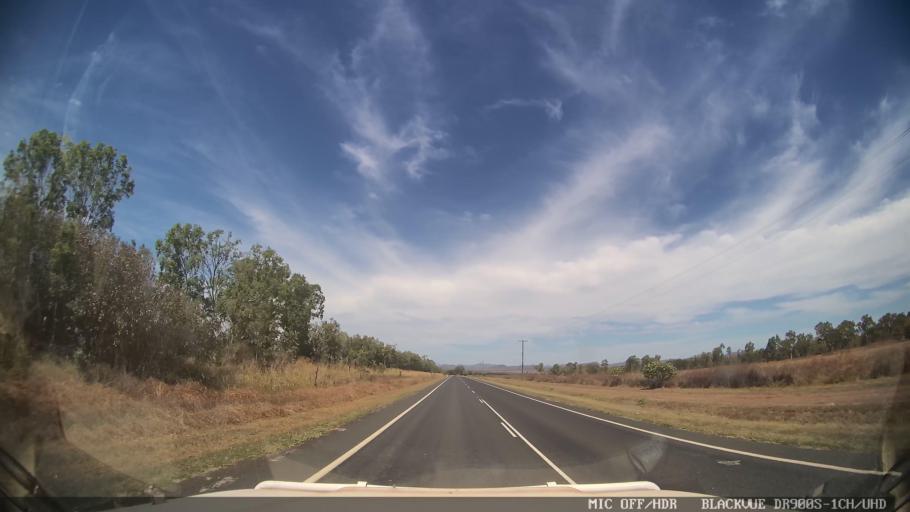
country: AU
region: Queensland
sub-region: Cook
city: Cooktown
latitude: -15.8393
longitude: 144.8531
